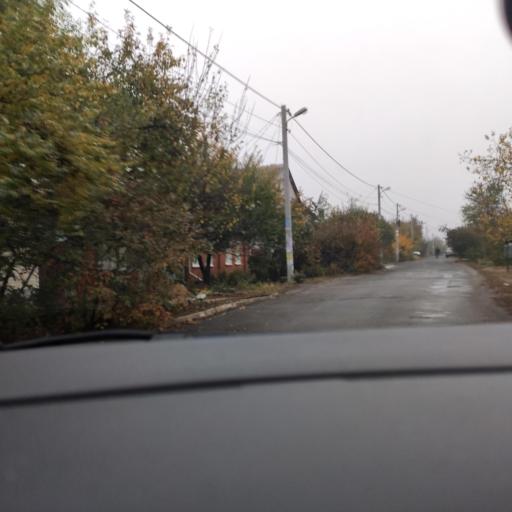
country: RU
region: Voronezj
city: Voronezh
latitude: 51.6448
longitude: 39.1860
